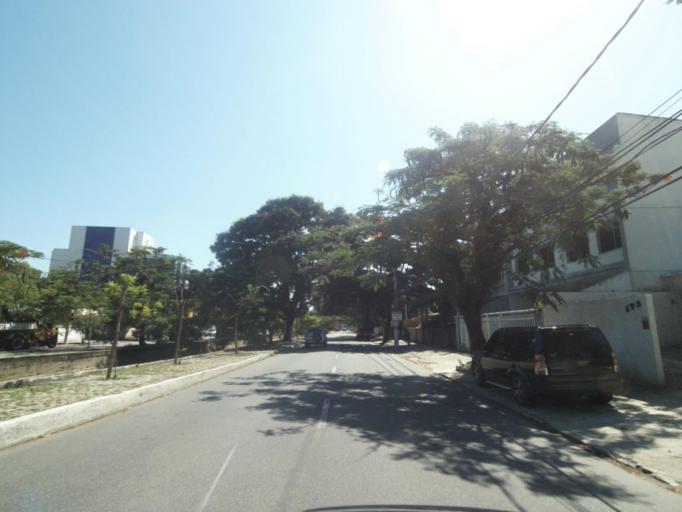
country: BR
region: Rio de Janeiro
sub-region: Niteroi
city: Niteroi
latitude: -22.9144
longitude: -43.0923
